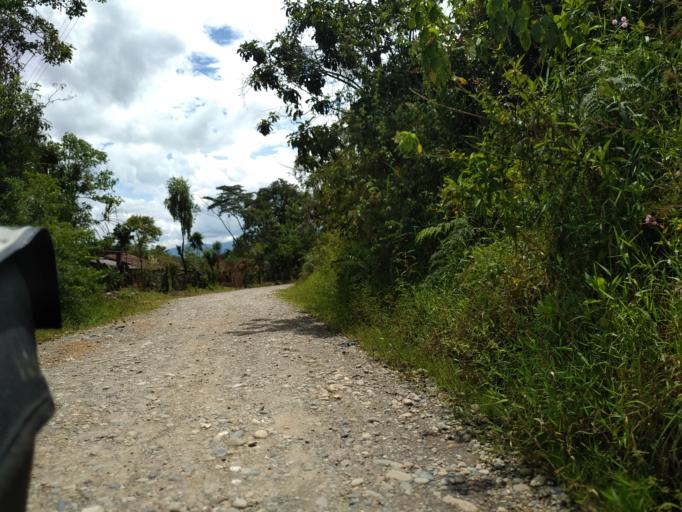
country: CO
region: Santander
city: Oiba
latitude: 6.1922
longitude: -73.1807
